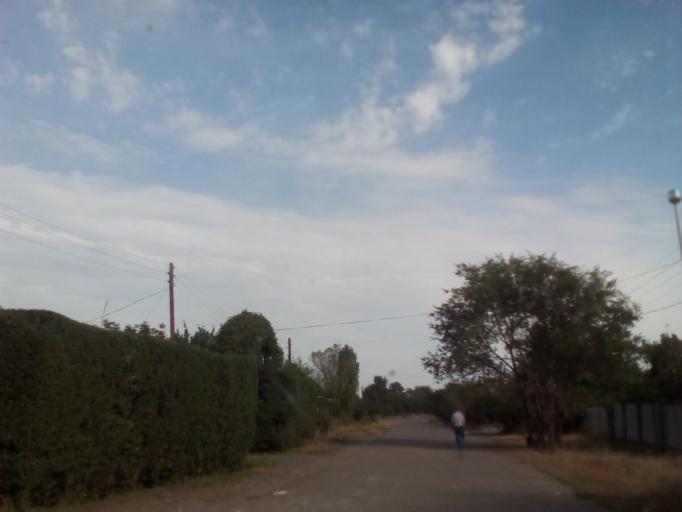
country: KZ
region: Almaty Oblysy
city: Burunday
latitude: 43.1668
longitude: 76.4050
